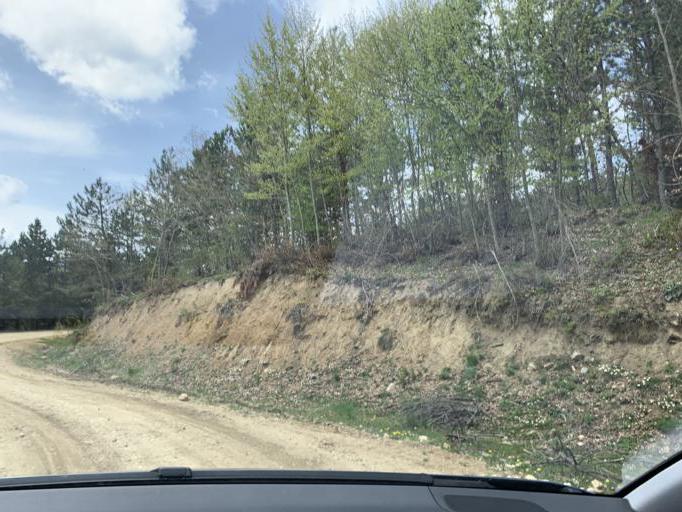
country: TR
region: Bolu
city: Bolu
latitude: 40.8342
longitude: 31.6721
